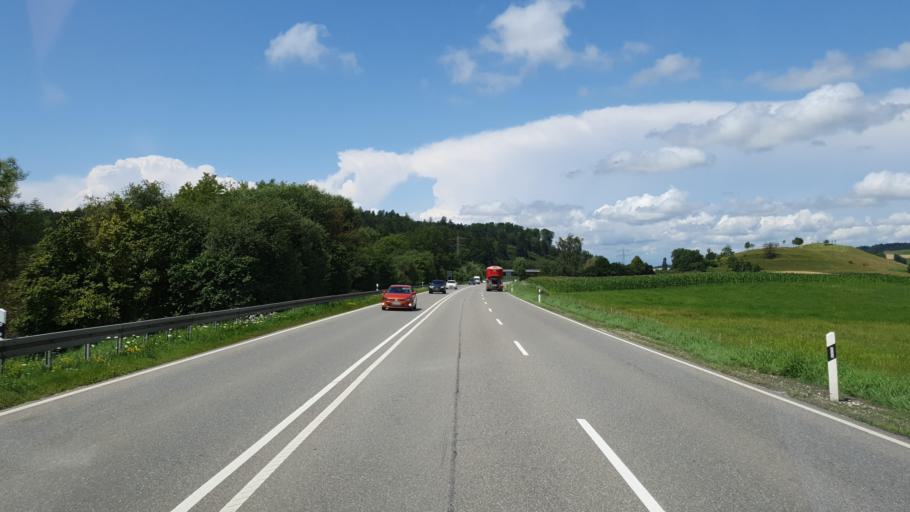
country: DE
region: Baden-Wuerttemberg
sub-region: Tuebingen Region
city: Sipplingen
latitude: 47.8034
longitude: 9.1272
